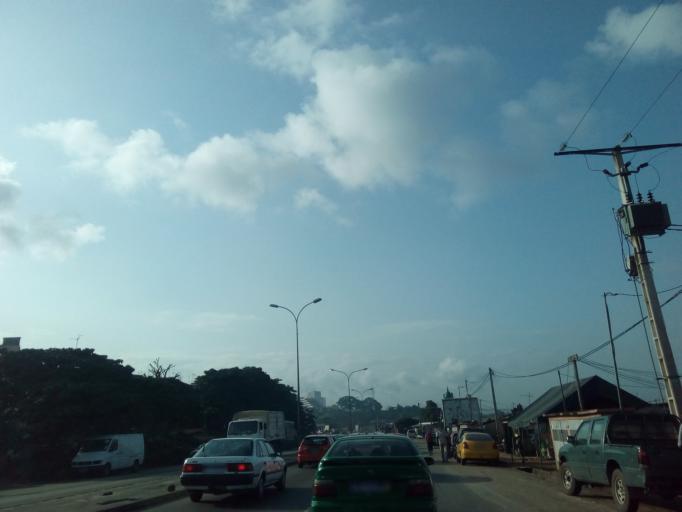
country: CI
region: Lagunes
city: Abidjan
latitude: 5.3433
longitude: -4.0368
